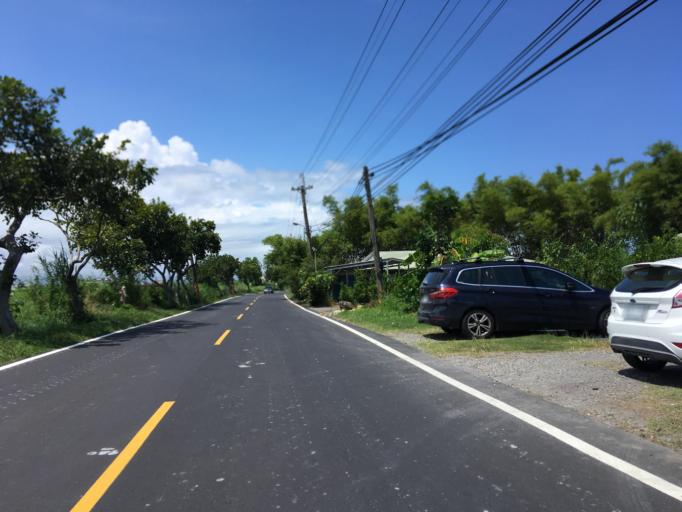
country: TW
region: Taiwan
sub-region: Yilan
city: Yilan
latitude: 24.6842
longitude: 121.8083
